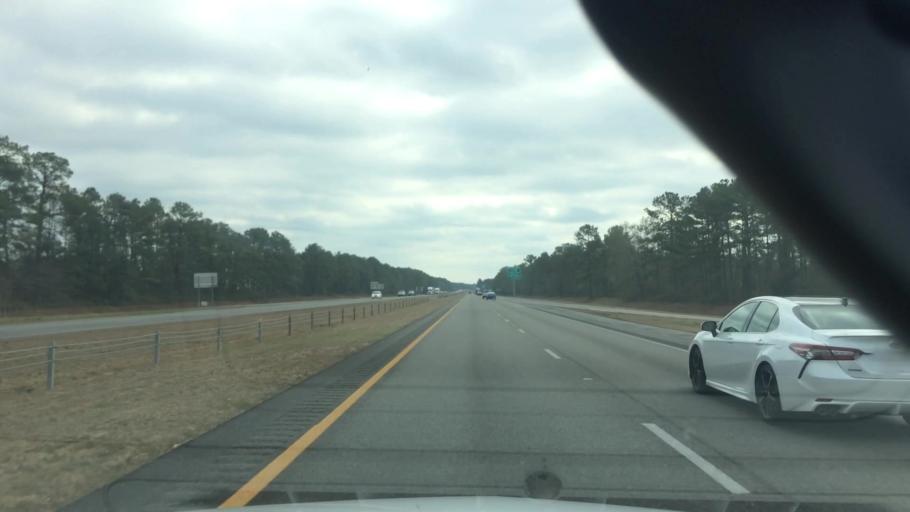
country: US
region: North Carolina
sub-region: New Hanover County
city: Castle Hayne
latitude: 34.3496
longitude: -77.8835
